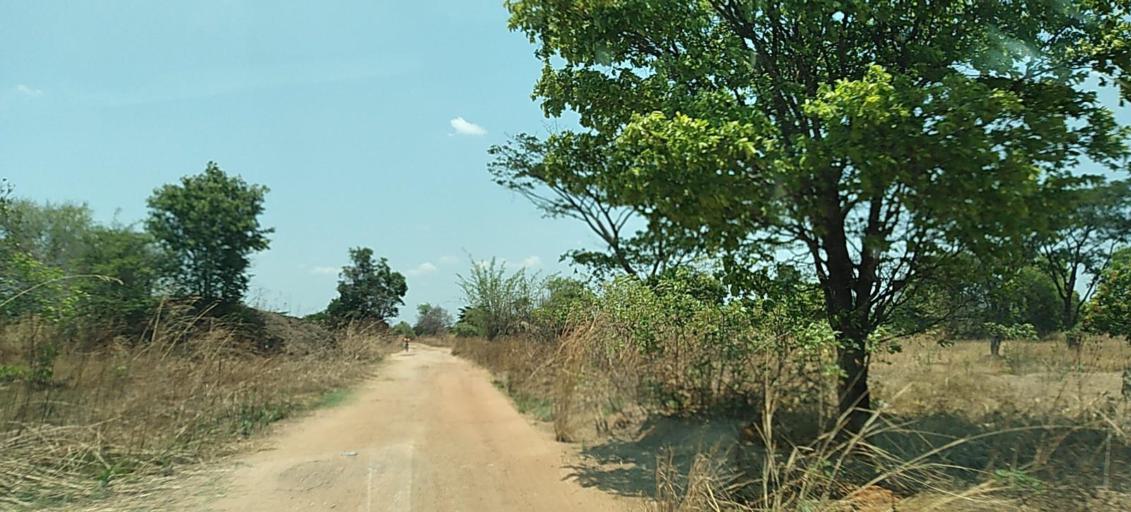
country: ZM
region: Copperbelt
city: Luanshya
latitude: -13.0864
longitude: 28.4058
